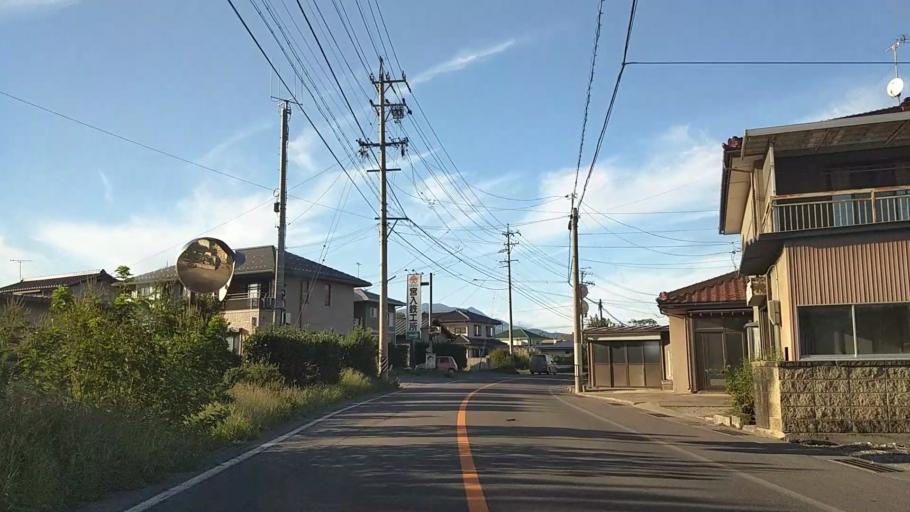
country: JP
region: Nagano
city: Nagano-shi
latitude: 36.5874
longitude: 138.1982
